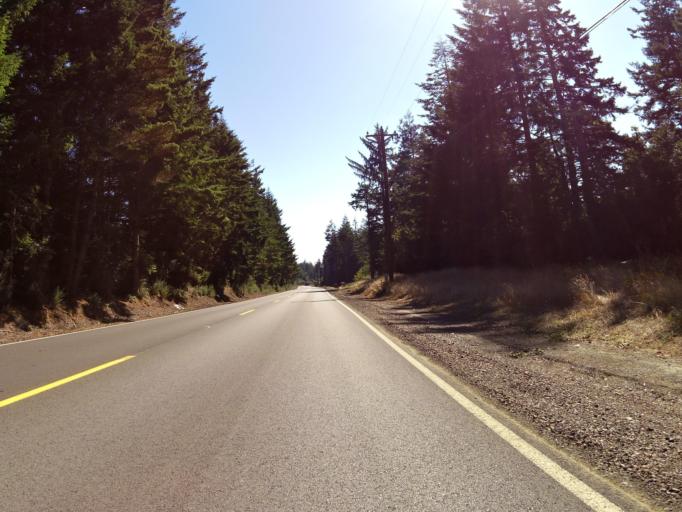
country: US
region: Oregon
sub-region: Coos County
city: Bandon
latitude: 43.1996
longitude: -124.3661
